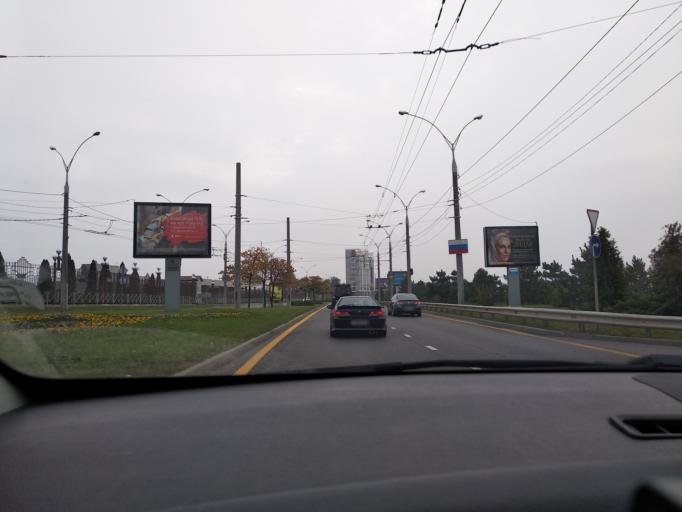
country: RU
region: Krasnodarskiy
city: Krasnodar
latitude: 45.0364
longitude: 38.9544
